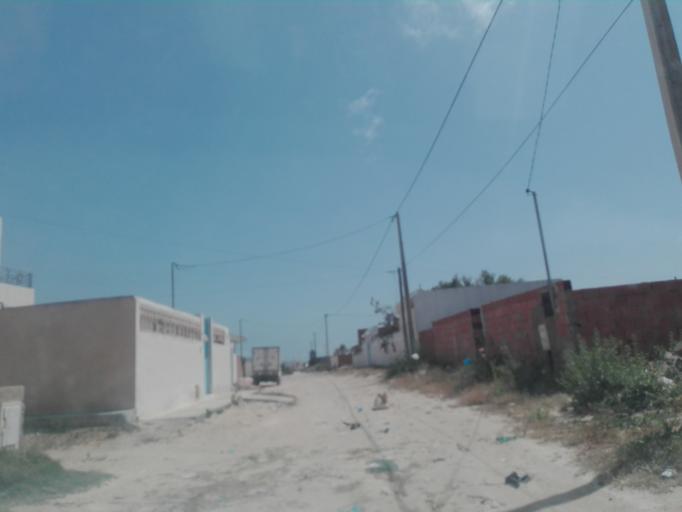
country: TN
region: Safaqis
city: Al Qarmadah
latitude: 34.6526
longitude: 11.0406
